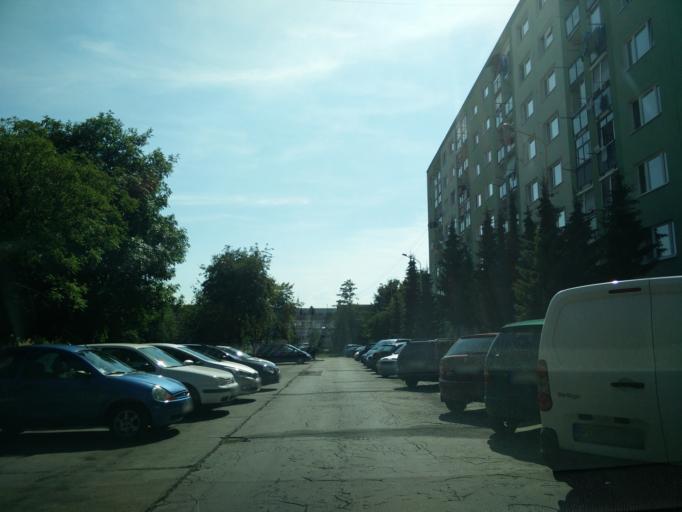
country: SK
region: Nitriansky
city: Prievidza
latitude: 48.7773
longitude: 18.6441
